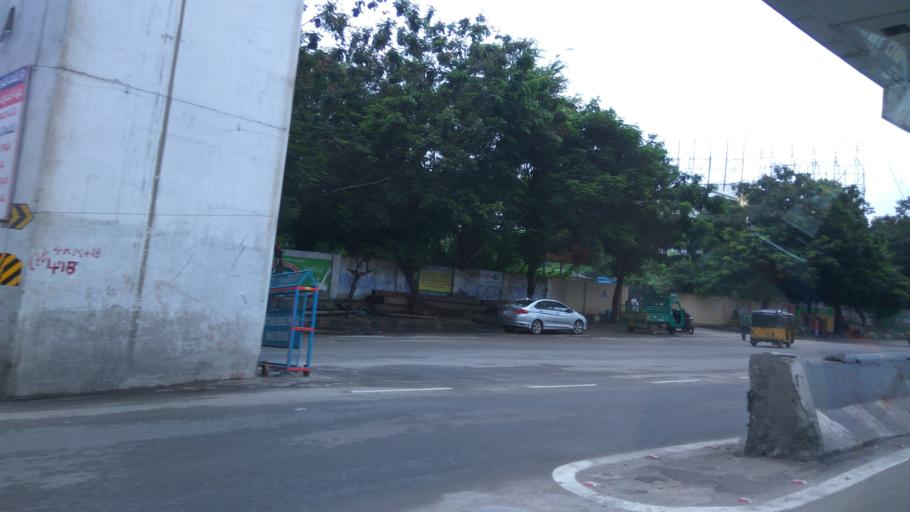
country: IN
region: Telangana
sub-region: Rangareddi
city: Quthbullapur
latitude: 17.4447
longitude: 78.4673
